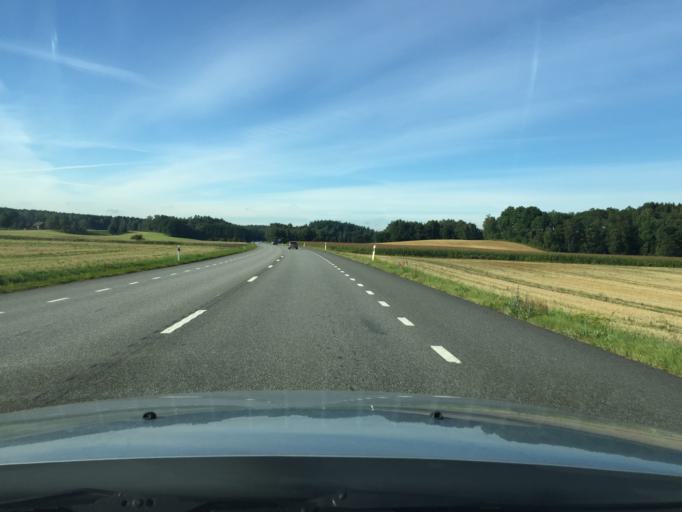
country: SE
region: Skane
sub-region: Hassleholms Kommun
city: Sosdala
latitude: 56.0259
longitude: 13.6756
